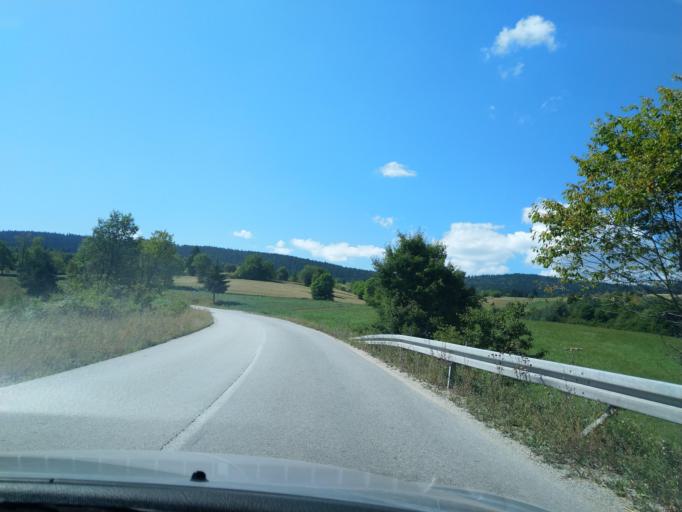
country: RS
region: Central Serbia
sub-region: Zlatiborski Okrug
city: Nova Varos
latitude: 43.4247
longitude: 19.8272
